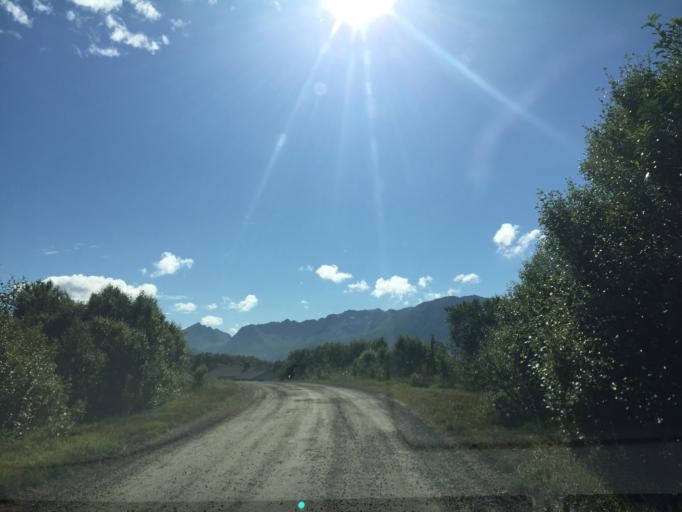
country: NO
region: Nordland
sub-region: Vagan
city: Kabelvag
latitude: 68.3556
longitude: 14.4488
